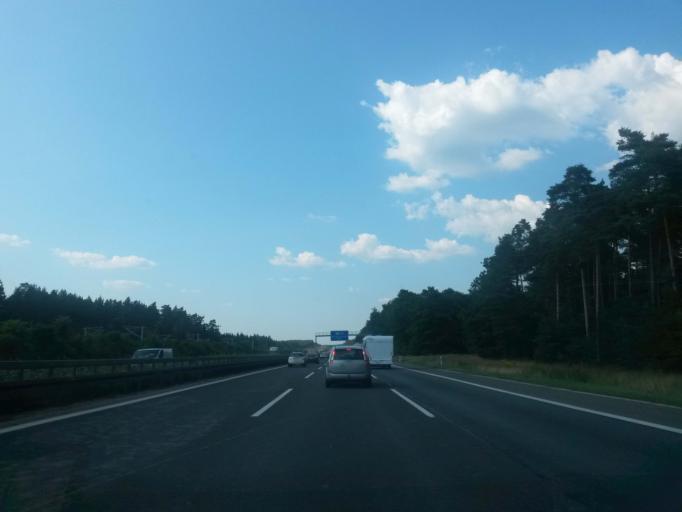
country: DE
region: Bavaria
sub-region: Regierungsbezirk Mittelfranken
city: Schwarzenbruck
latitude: 49.3207
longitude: 11.2067
